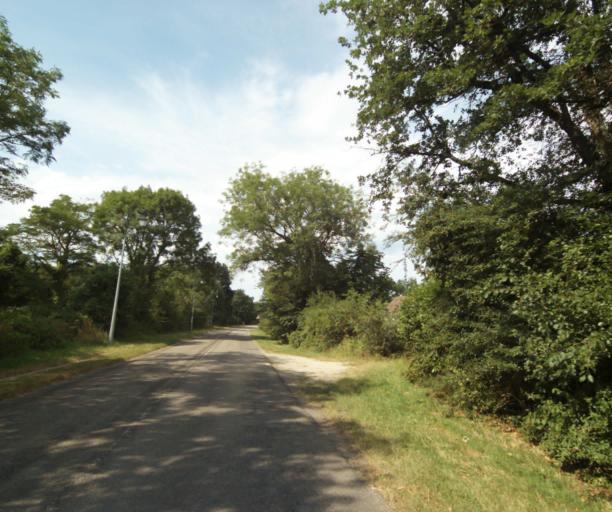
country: FR
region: Ile-de-France
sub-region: Departement de Seine-et-Marne
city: Acheres-la-Foret
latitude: 48.3579
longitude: 2.5626
